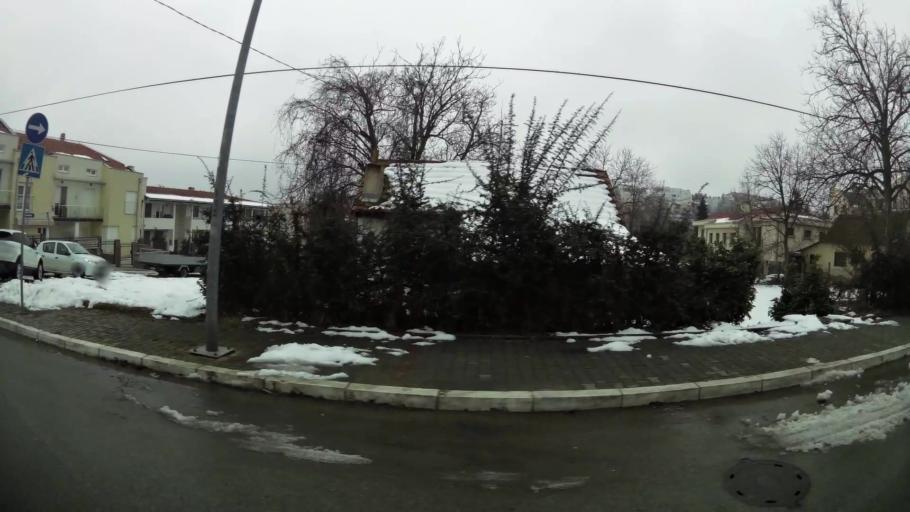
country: RS
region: Central Serbia
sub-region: Belgrade
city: Savski Venac
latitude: 44.7634
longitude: 20.4591
